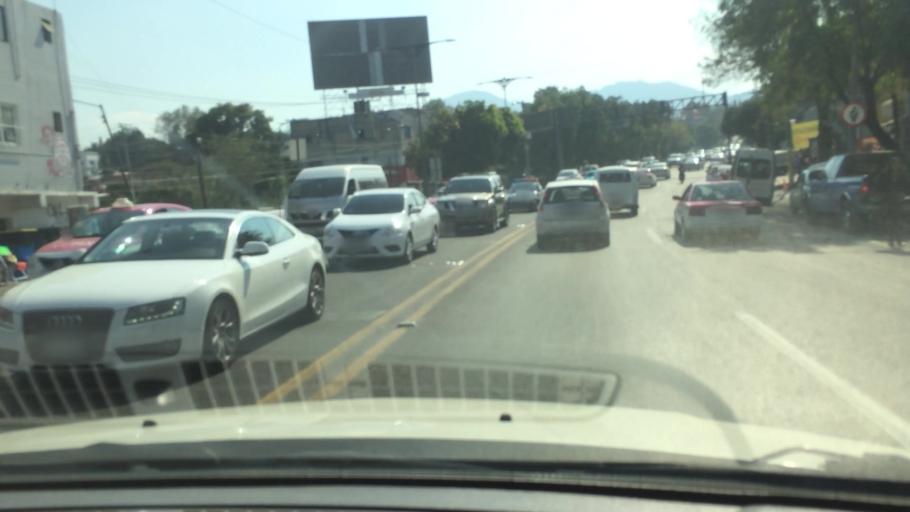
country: MX
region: Mexico City
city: Tlalpan
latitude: 19.2662
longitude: -99.1710
